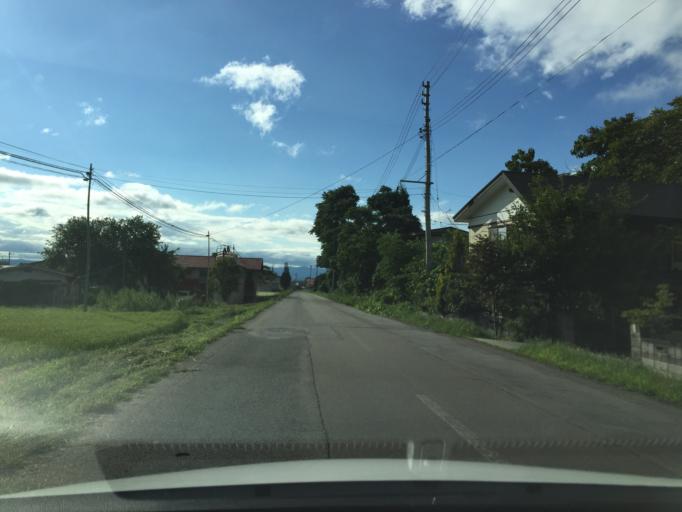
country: JP
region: Yamagata
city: Takahata
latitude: 37.9528
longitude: 140.2022
